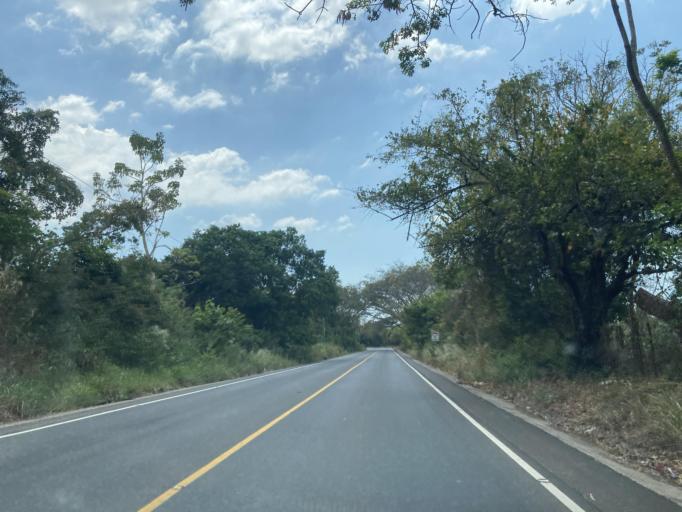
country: GT
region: Santa Rosa
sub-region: Municipio de Taxisco
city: Taxisco
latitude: 14.0686
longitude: -90.4714
